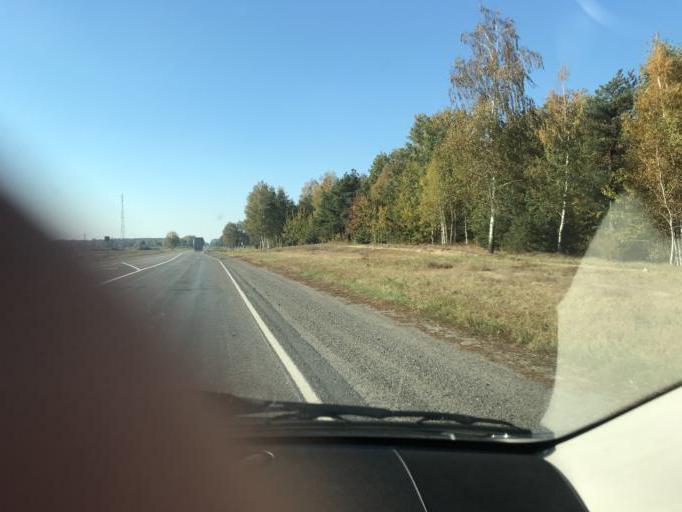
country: BY
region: Brest
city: Davyd-Haradok
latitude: 52.2438
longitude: 27.1589
